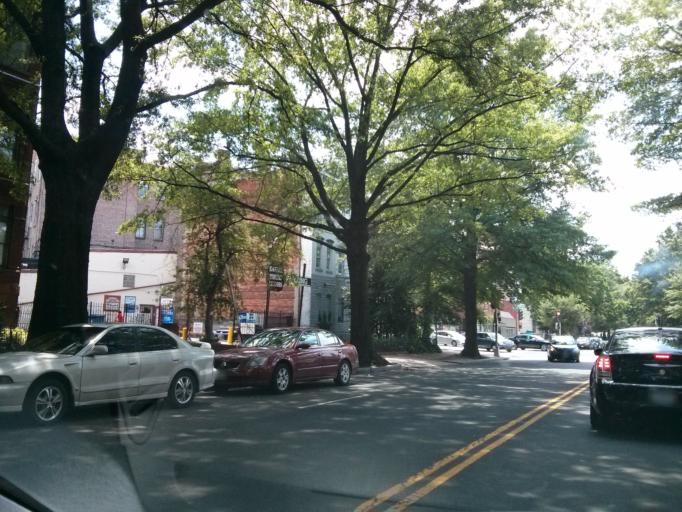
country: US
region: Washington, D.C.
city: Washington, D.C.
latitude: 38.9091
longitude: -77.0314
